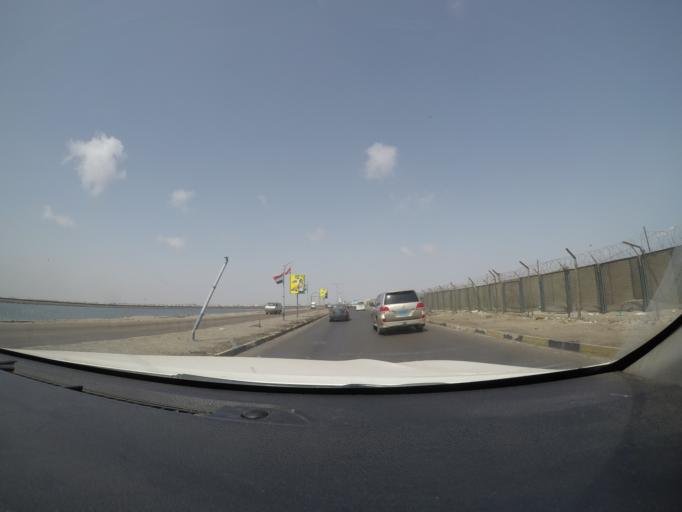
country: YE
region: Aden
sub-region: Khur Maksar
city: Khawr Maksar
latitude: 12.8295
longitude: 45.0307
